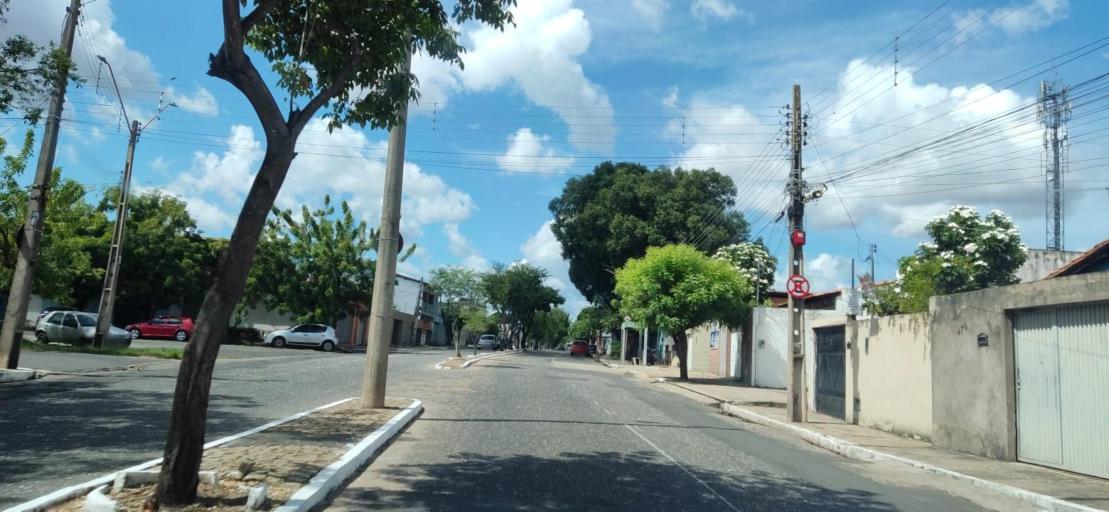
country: BR
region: Maranhao
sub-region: Timon
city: Timon
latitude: -5.0818
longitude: -42.8265
